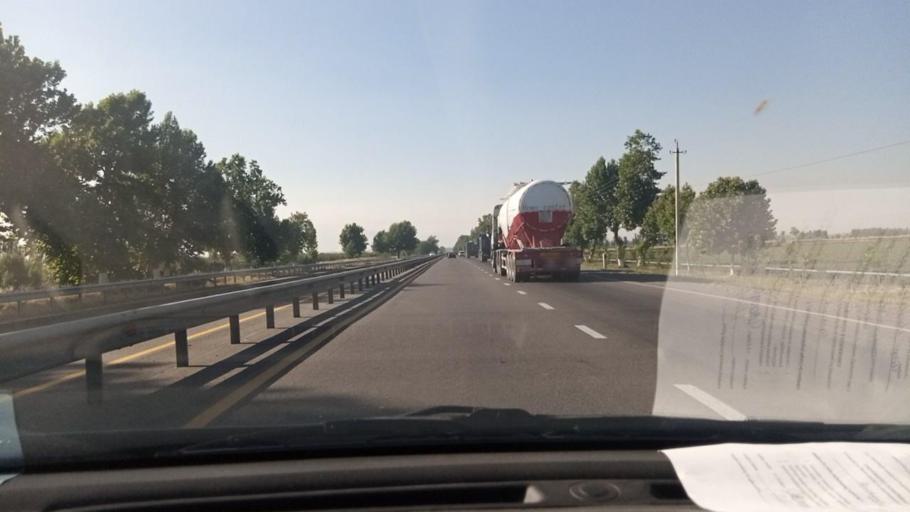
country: UZ
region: Toshkent Shahri
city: Bektemir
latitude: 41.1746
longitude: 69.4113
